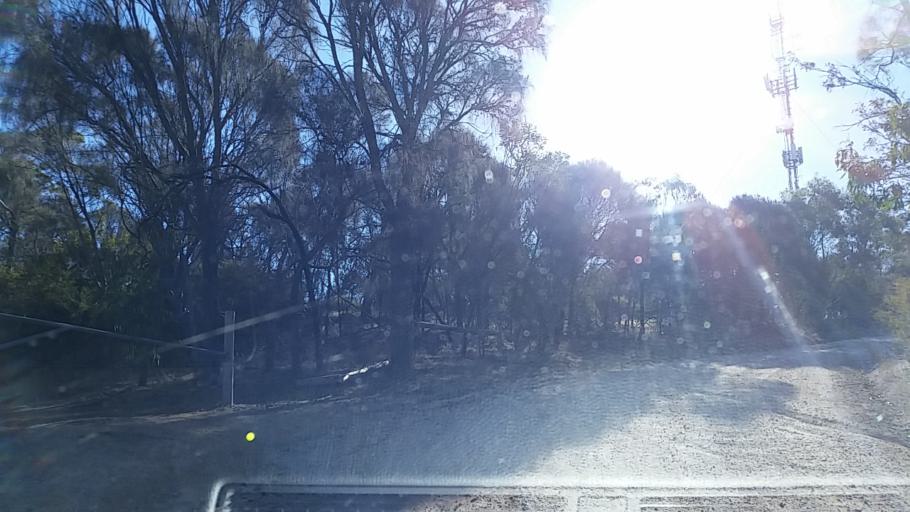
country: AU
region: South Australia
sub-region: Mount Barker
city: Nairne
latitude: -35.0673
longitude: 138.9225
